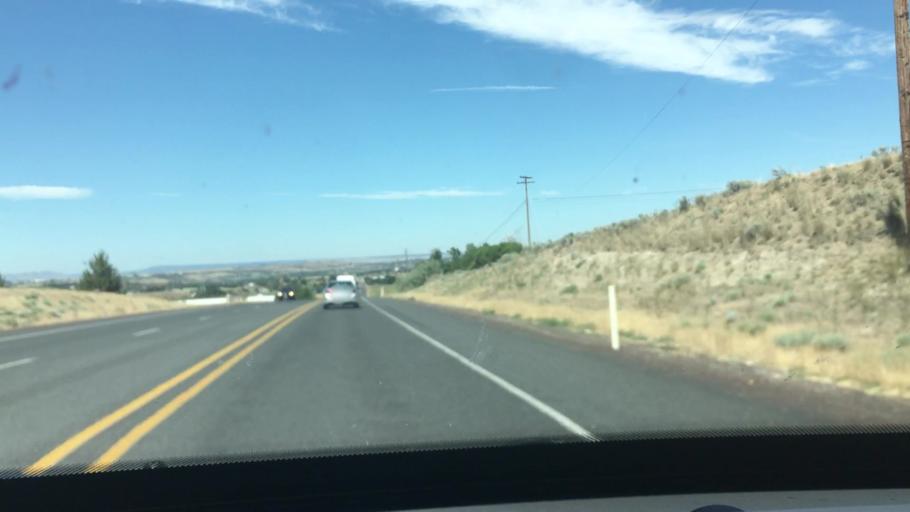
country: US
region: Oregon
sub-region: Jefferson County
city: Madras
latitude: 44.5806
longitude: -121.1551
